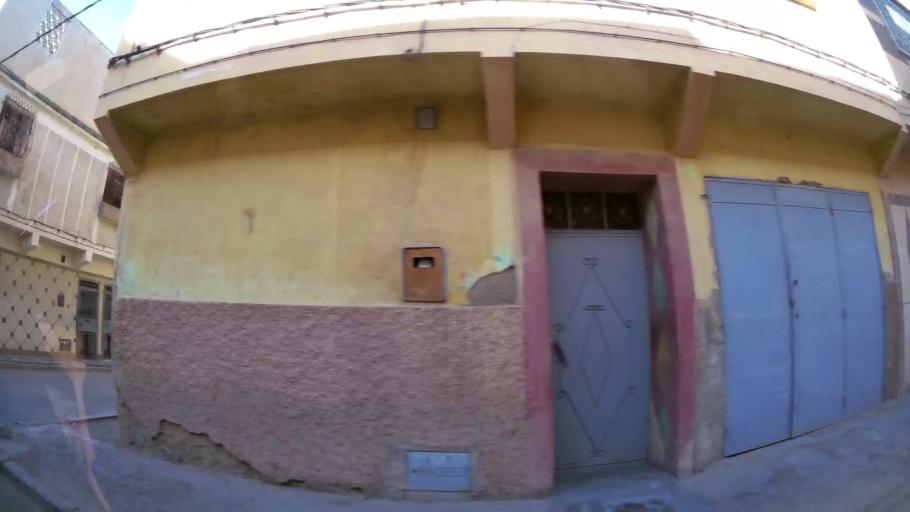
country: MA
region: Oriental
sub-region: Oujda-Angad
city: Oujda
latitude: 34.6738
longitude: -1.8985
